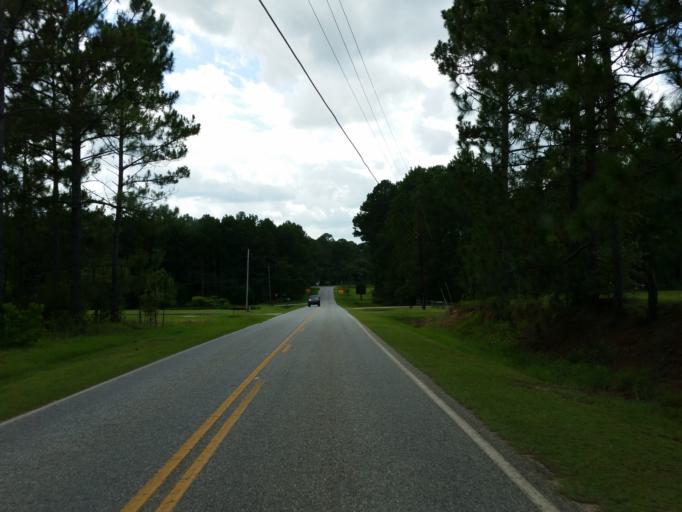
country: US
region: Georgia
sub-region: Tift County
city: Unionville
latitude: 31.3573
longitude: -83.5019
